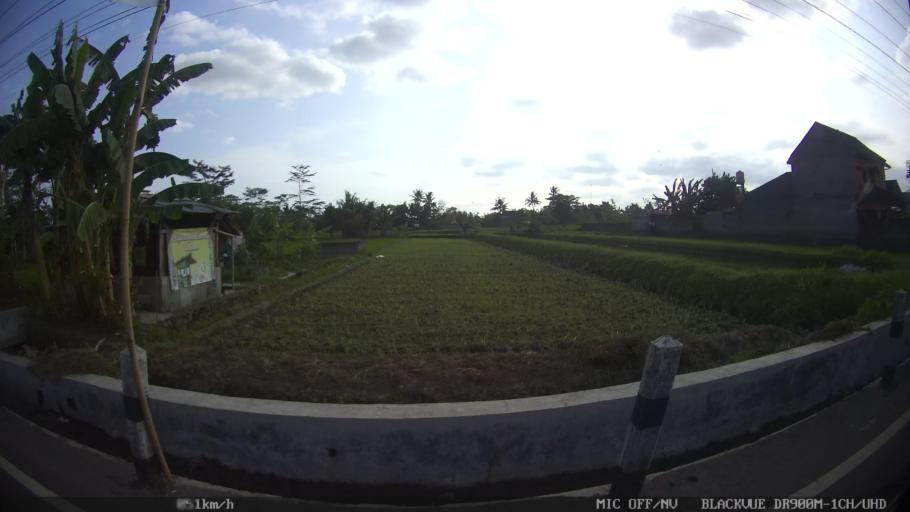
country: ID
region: Central Java
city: Candi Prambanan
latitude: -7.7074
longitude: 110.4685
